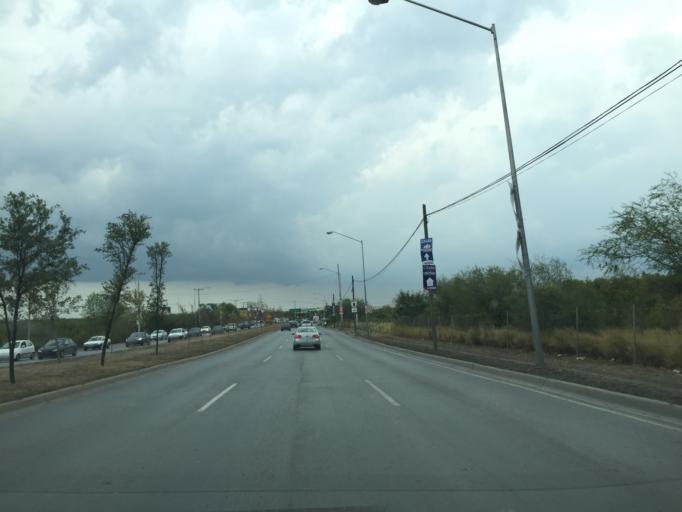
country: MX
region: Nuevo Leon
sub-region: Apodaca
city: Loma la Paz
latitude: 25.6844
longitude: -100.1666
